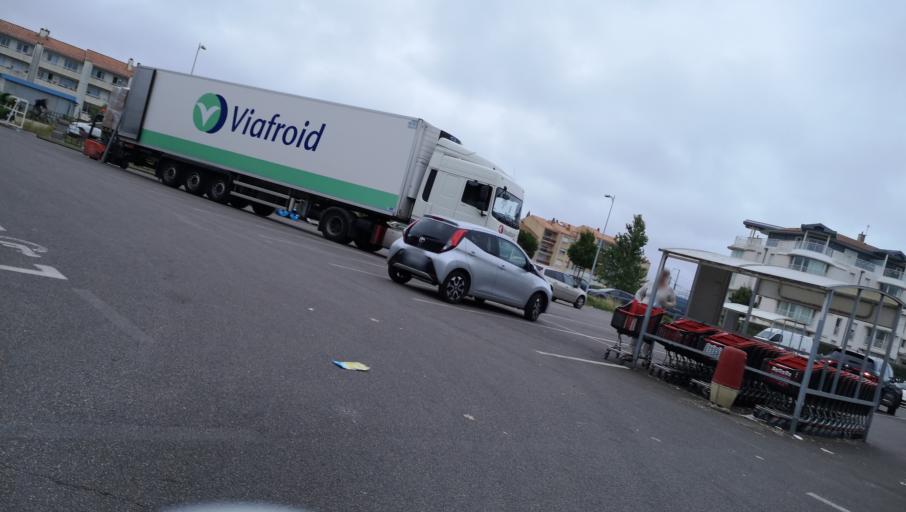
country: FR
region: Pays de la Loire
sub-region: Departement de la Vendee
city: Les Sables-d'Olonne
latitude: 46.5032
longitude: -1.7854
